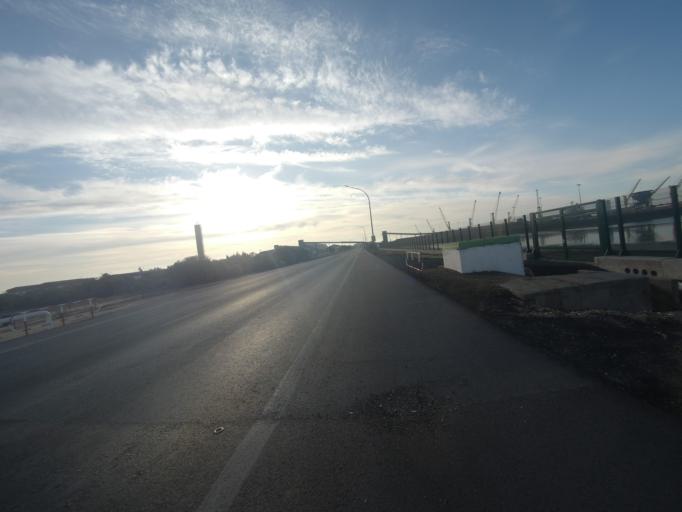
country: ES
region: Andalusia
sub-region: Provincia de Huelva
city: Punta Umbria
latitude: 37.2010
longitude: -6.9361
